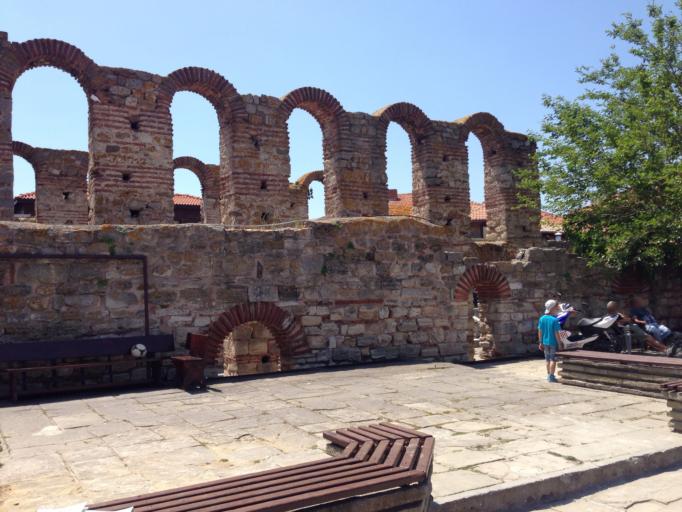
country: BG
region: Burgas
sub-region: Obshtina Nesebur
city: Nesebar
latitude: 42.6593
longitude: 27.7362
